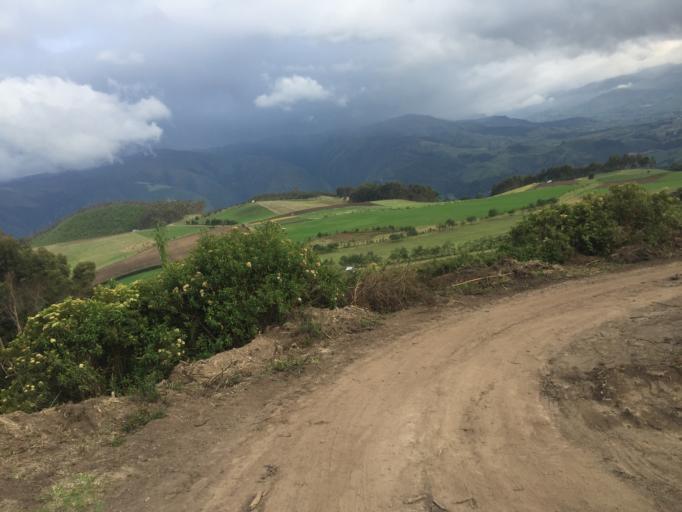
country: EC
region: Imbabura
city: Ibarra
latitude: 0.2278
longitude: -78.1207
